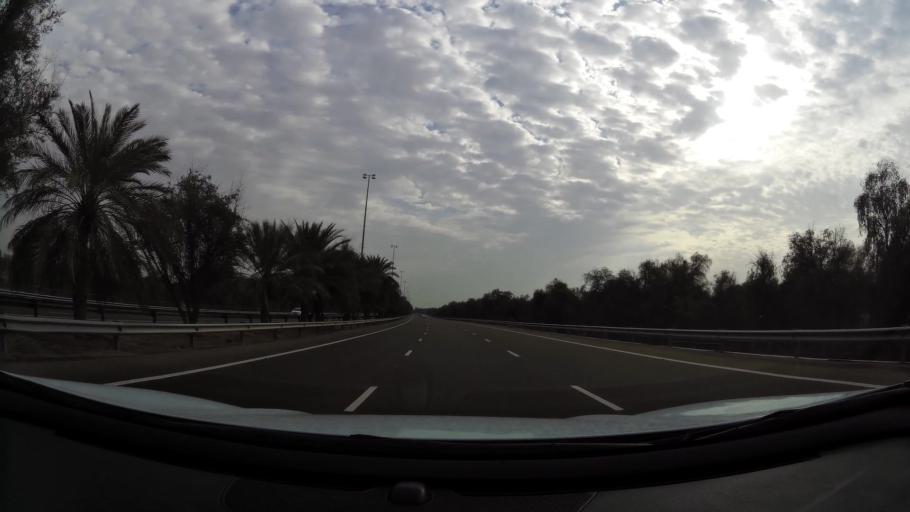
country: AE
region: Abu Dhabi
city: Al Ain
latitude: 24.1675
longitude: 55.2744
